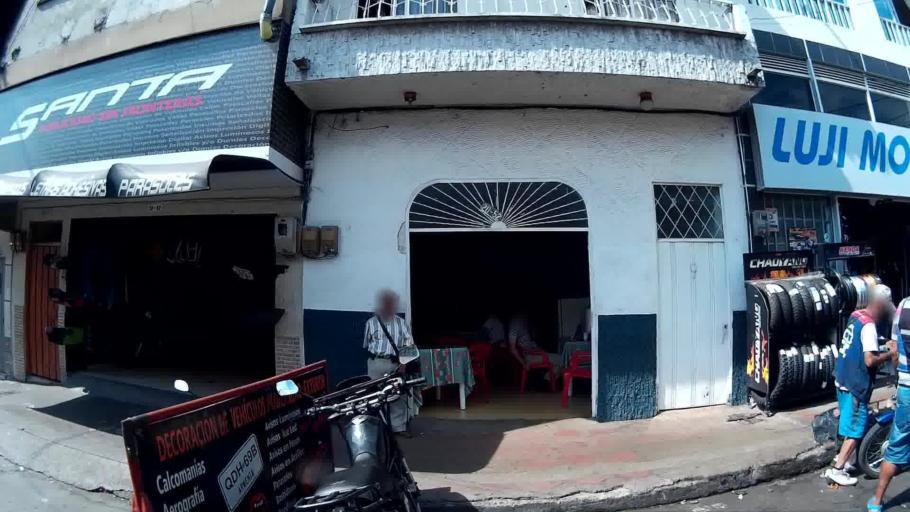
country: CO
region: Quindio
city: Armenia
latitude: 4.5391
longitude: -75.6732
